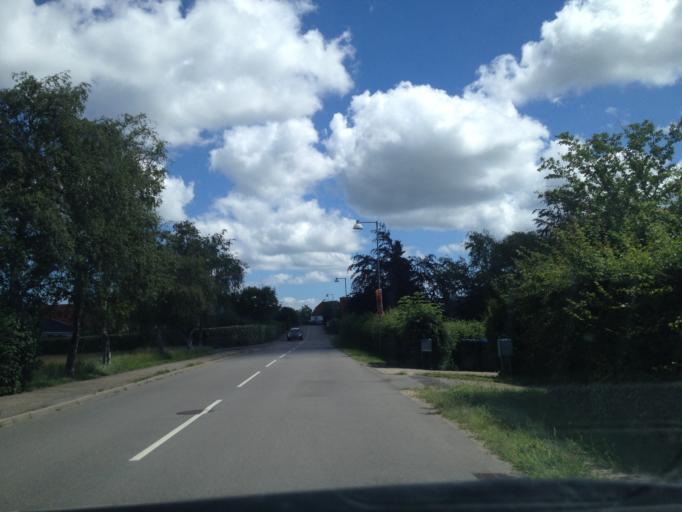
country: DK
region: Zealand
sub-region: Odsherred Kommune
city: Hojby
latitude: 55.9106
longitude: 11.5887
